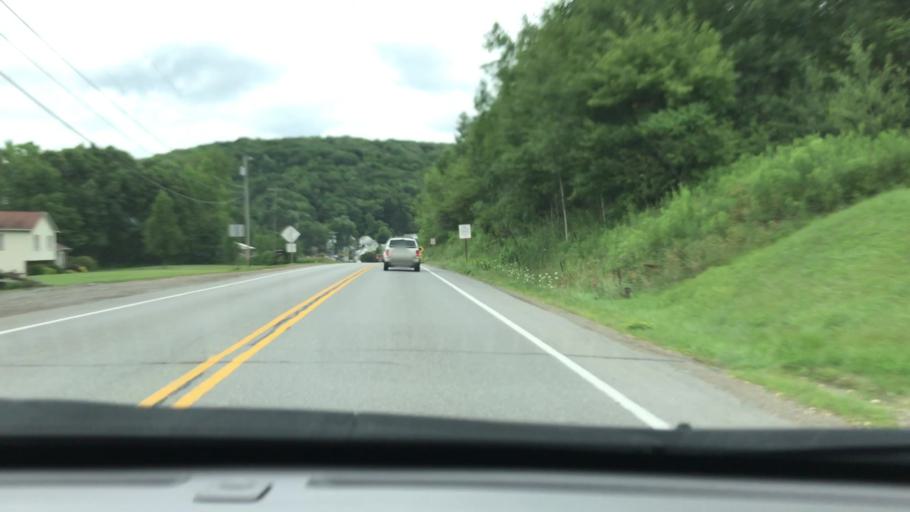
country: US
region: Pennsylvania
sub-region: Elk County
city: Johnsonburg
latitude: 41.4757
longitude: -78.6703
